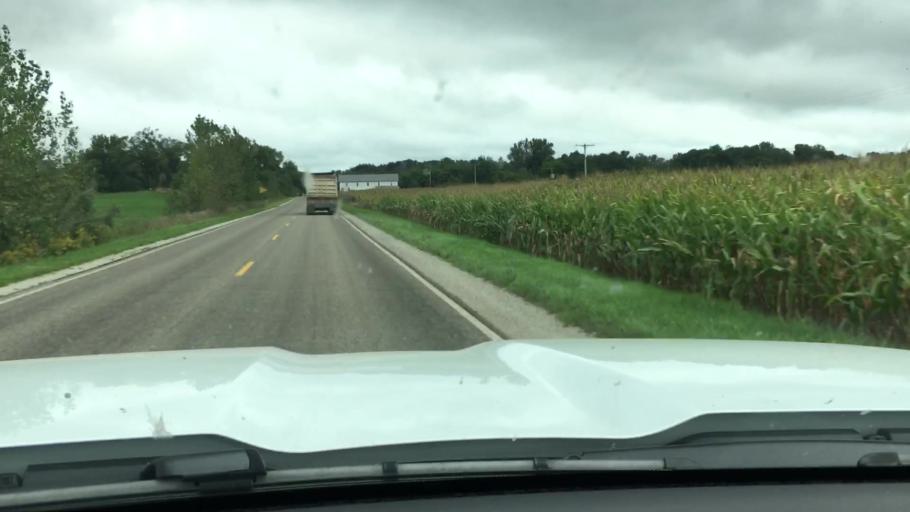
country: US
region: Michigan
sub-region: Montcalm County
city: Carson City
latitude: 43.2450
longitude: -84.7775
